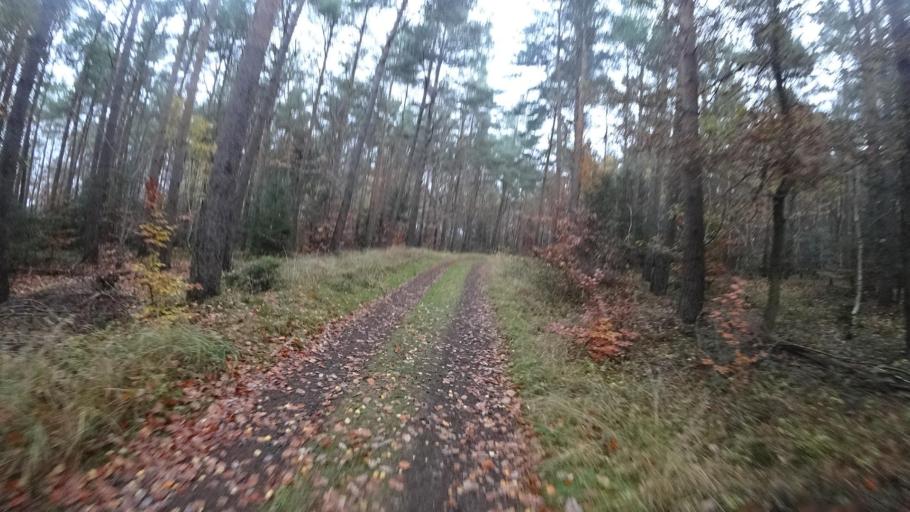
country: DE
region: Rheinland-Pfalz
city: Schalkenbach
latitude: 50.5068
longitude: 7.1229
